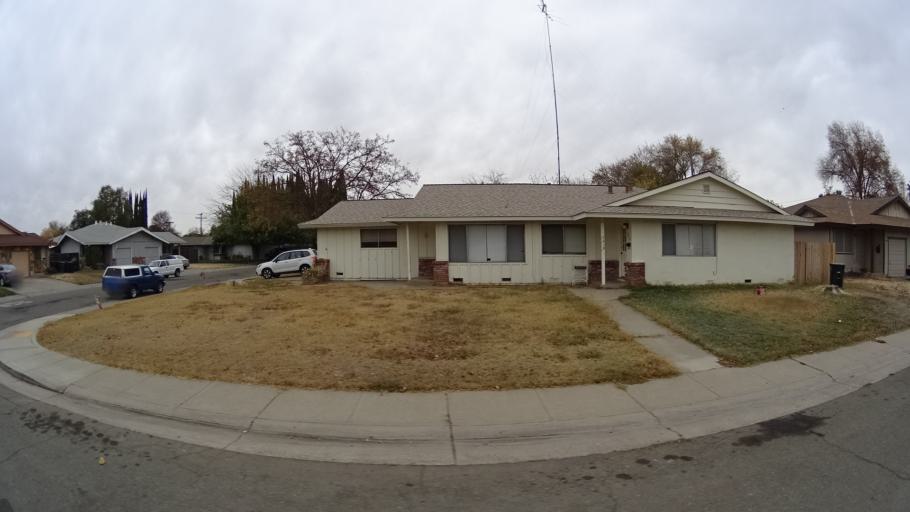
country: US
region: California
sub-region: Sacramento County
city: Citrus Heights
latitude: 38.6976
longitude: -121.3049
